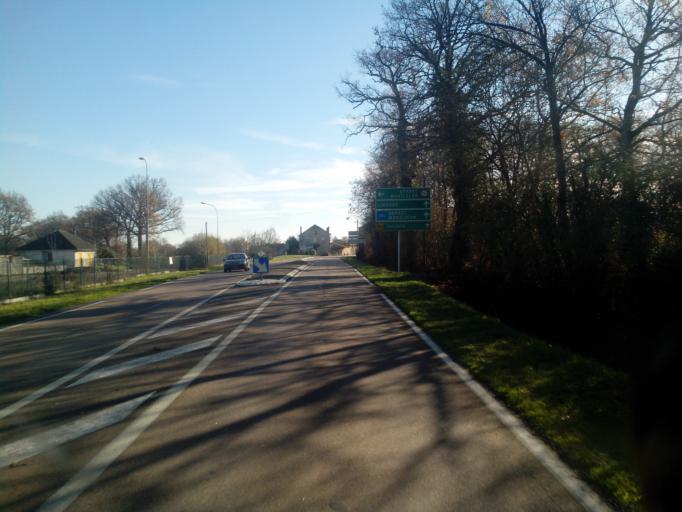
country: FR
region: Limousin
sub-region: Departement de la Haute-Vienne
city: Bussiere-Poitevine
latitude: 46.2417
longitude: 0.8914
